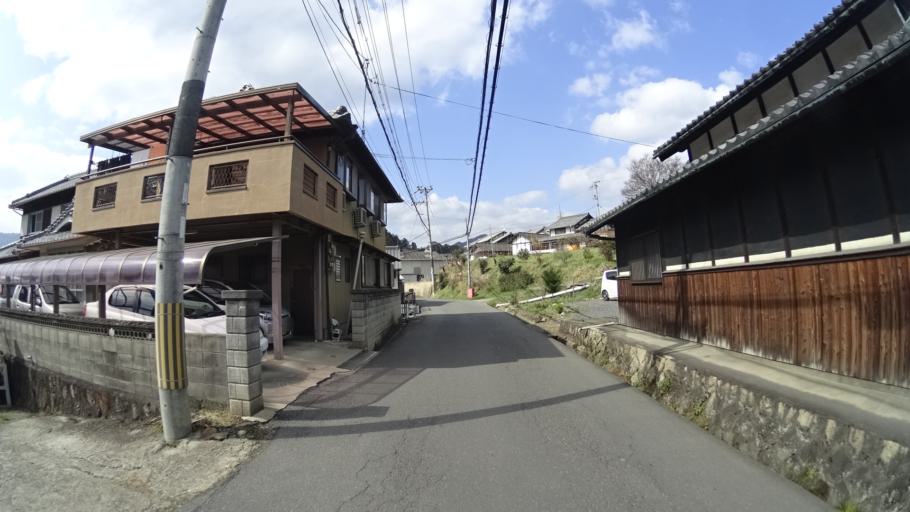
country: JP
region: Kyoto
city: Tanabe
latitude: 34.7892
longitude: 135.9050
